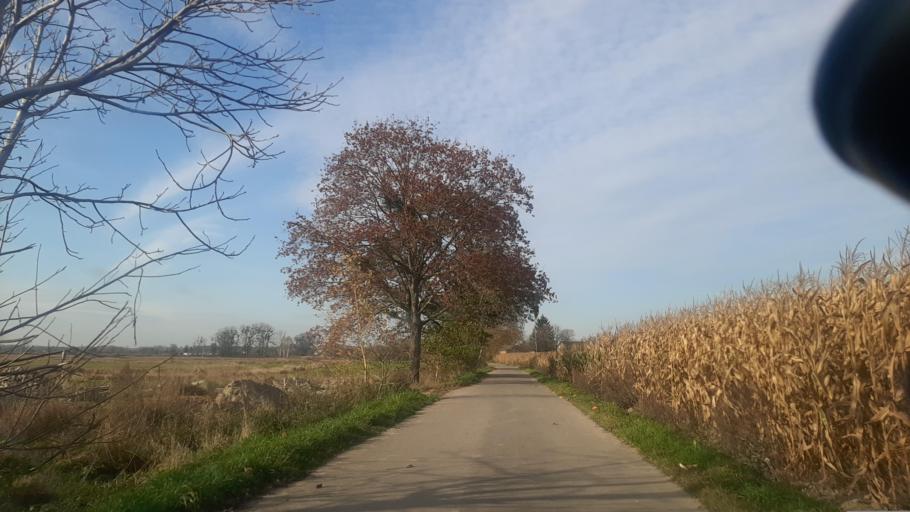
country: PL
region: Lublin Voivodeship
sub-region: Powiat pulawski
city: Markuszow
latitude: 51.3644
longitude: 22.2758
